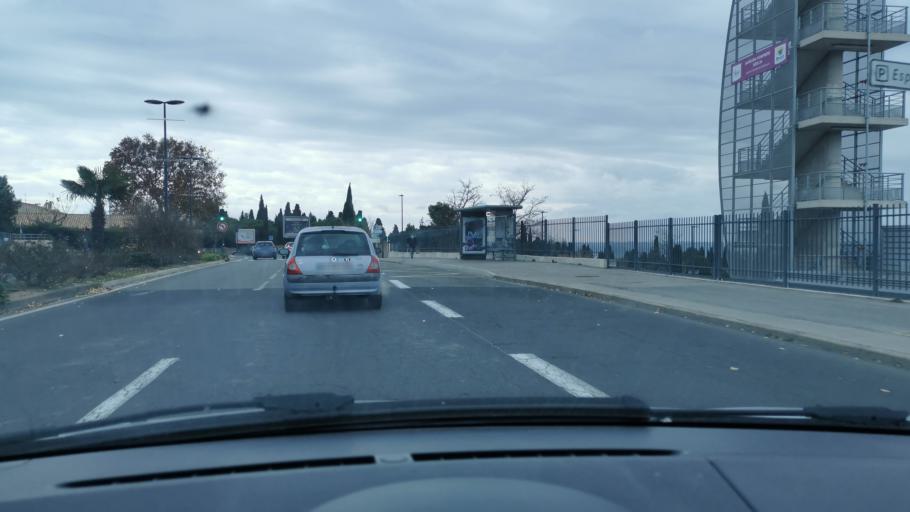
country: FR
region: Languedoc-Roussillon
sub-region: Departement de l'Herault
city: Sete
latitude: 43.4065
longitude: 3.6651
